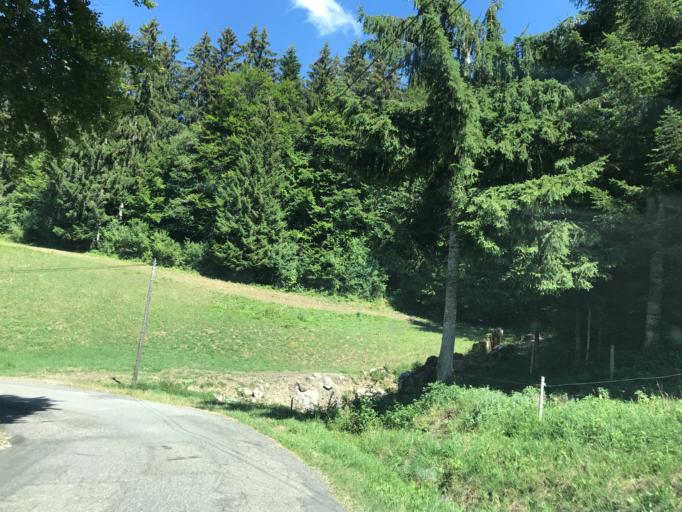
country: FR
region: Rhone-Alpes
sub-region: Departement de la Haute-Savoie
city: Thorens-Glieres
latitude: 45.9741
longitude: 6.2289
